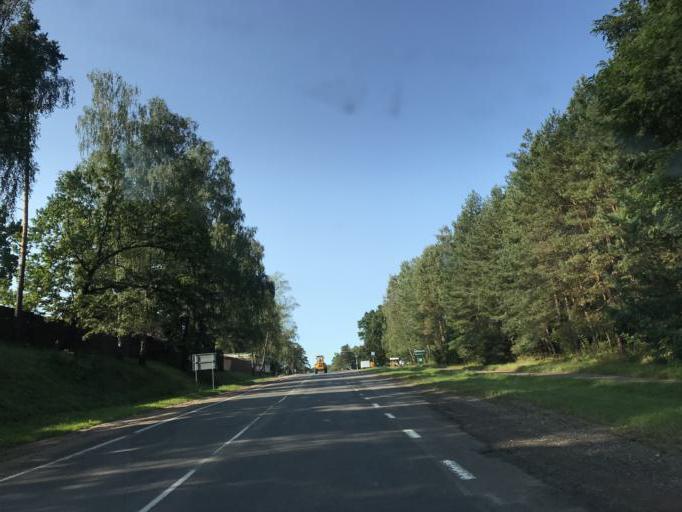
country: BY
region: Mogilev
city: Buynichy
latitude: 53.8119
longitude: 30.2284
